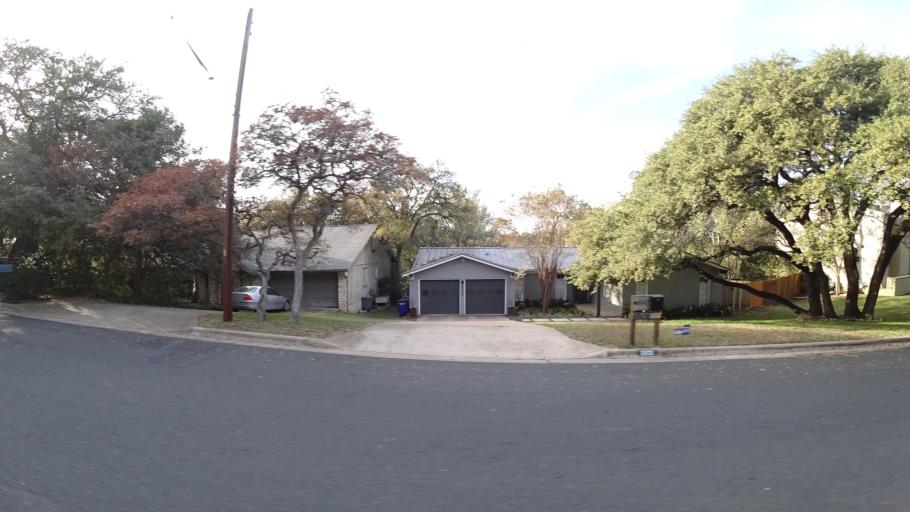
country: US
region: Texas
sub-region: Williamson County
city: Jollyville
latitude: 30.3845
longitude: -97.7518
